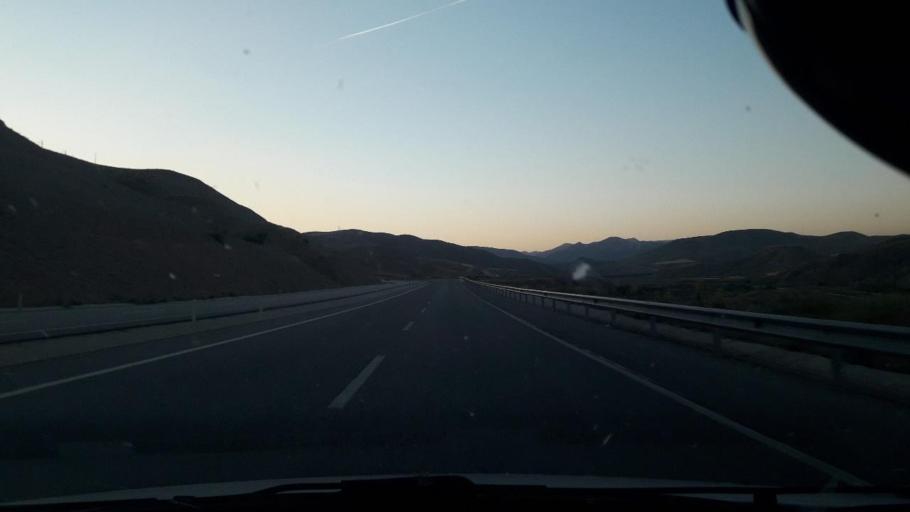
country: TR
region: Malatya
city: Yazihan
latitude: 38.6249
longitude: 38.1648
